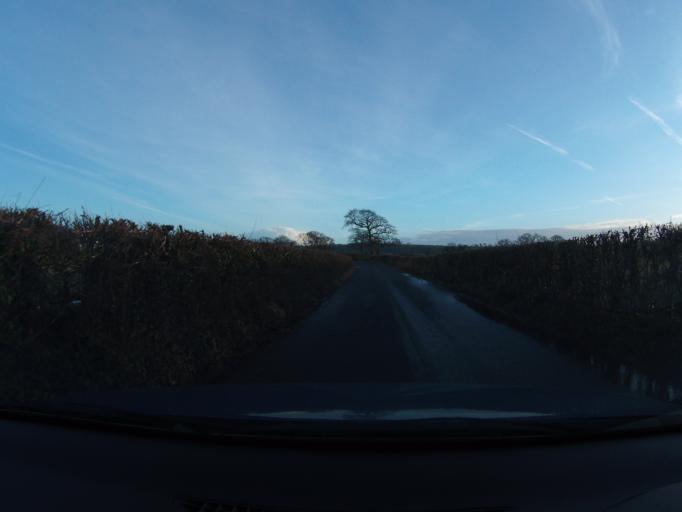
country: GB
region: England
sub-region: Isle of Wight
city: Brading
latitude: 50.6936
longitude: -1.1663
